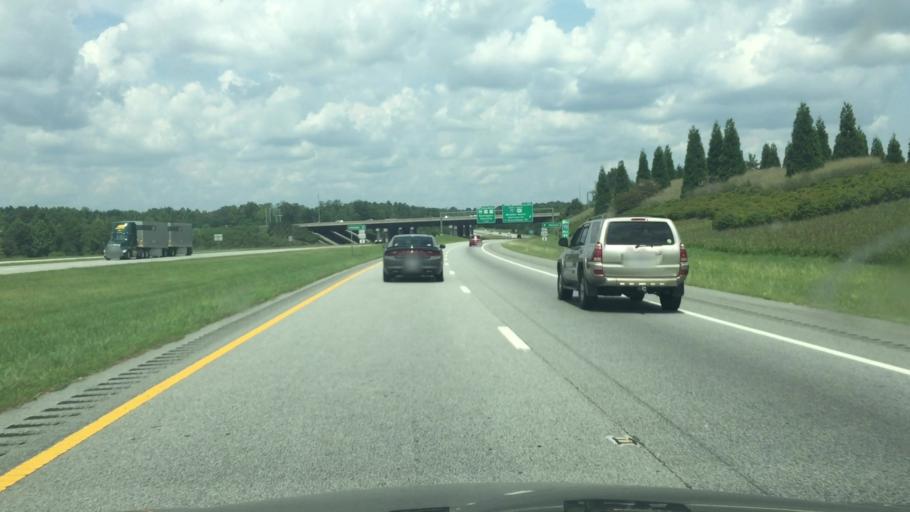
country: US
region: North Carolina
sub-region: Guilford County
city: Pleasant Garden
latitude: 35.9995
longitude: -79.8282
